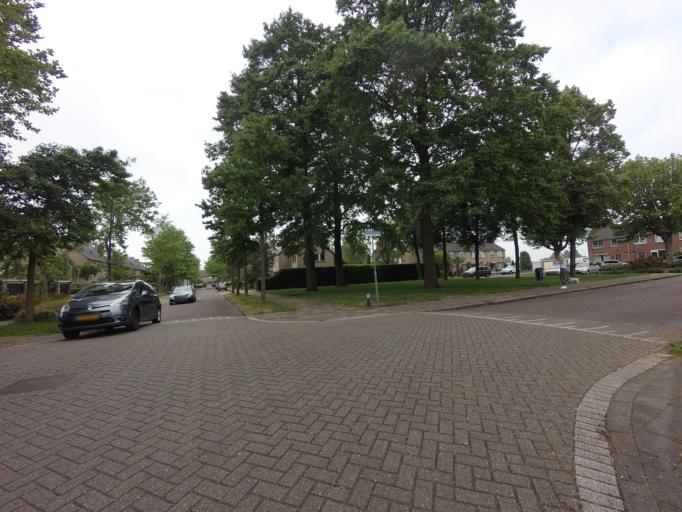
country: NL
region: Utrecht
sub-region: Stichtse Vecht
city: Spechtenkamp
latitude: 52.1102
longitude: 5.0115
